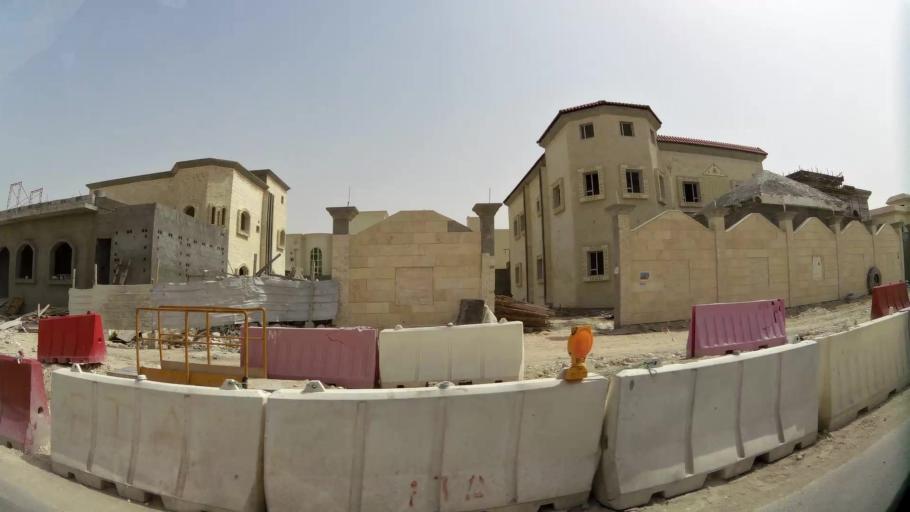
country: QA
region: Baladiyat ar Rayyan
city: Ar Rayyan
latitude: 25.2596
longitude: 51.3701
